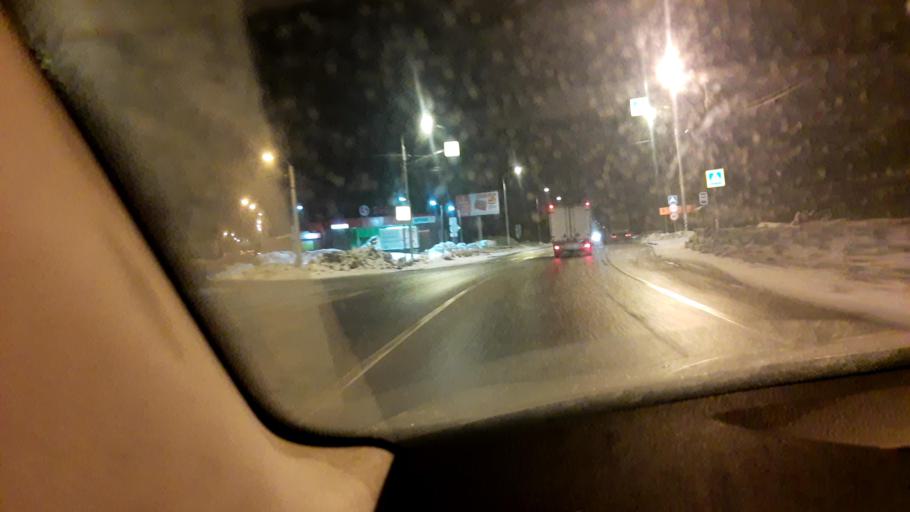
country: RU
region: Moskovskaya
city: Skoropuskovskiy
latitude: 56.3813
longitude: 38.1070
